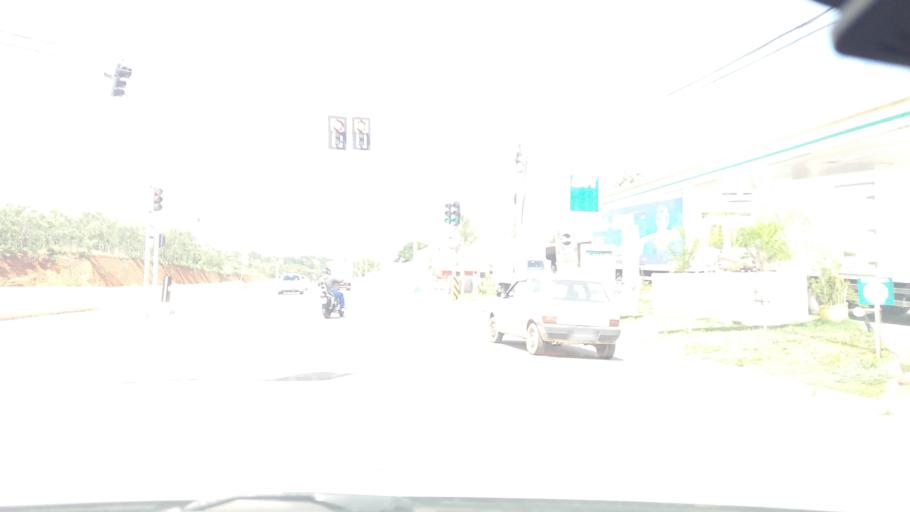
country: BR
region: Sao Paulo
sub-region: Atibaia
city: Atibaia
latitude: -23.1090
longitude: -46.5246
